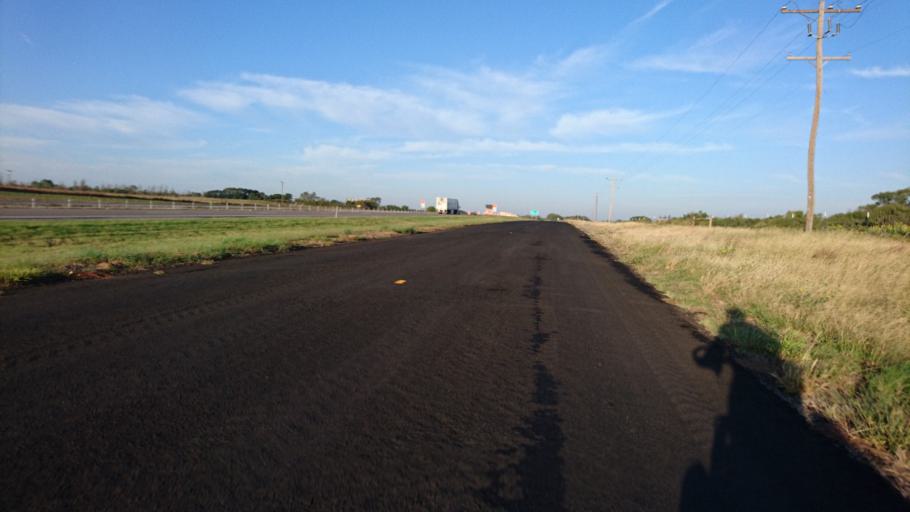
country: US
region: Oklahoma
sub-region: Beckham County
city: Sayre
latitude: 35.2625
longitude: -99.6973
